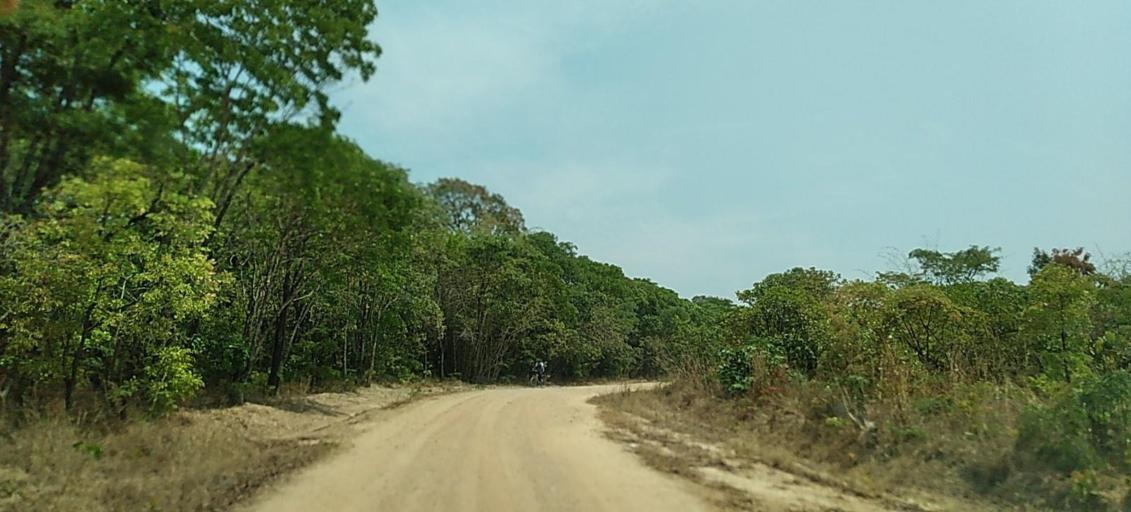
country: ZM
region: Copperbelt
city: Kalulushi
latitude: -12.9524
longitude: 28.1500
